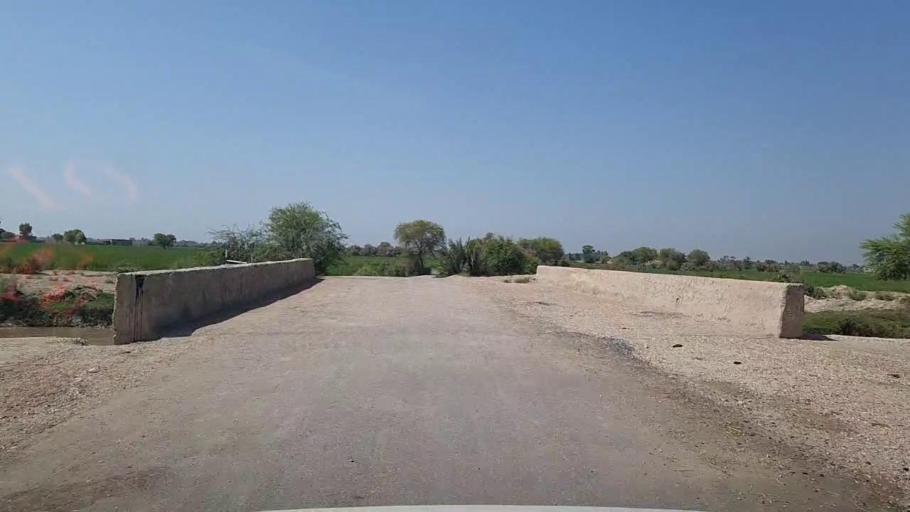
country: PK
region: Sindh
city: Kandhkot
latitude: 28.3234
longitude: 69.3376
